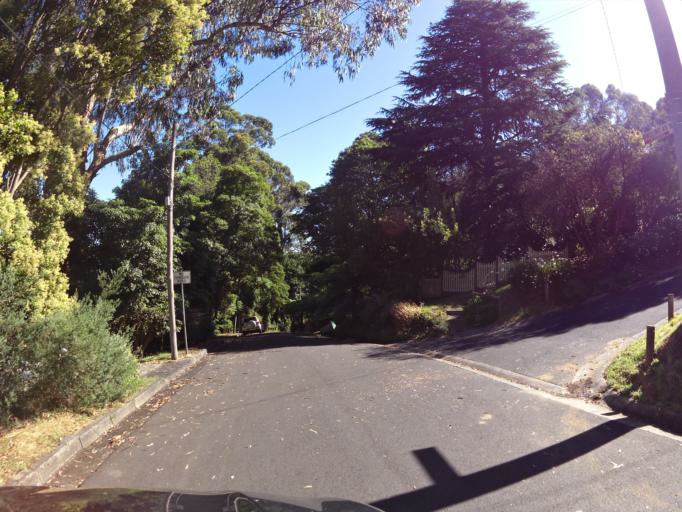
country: AU
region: Victoria
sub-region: Yarra Ranges
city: Tecoma
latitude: -37.9007
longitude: 145.3429
